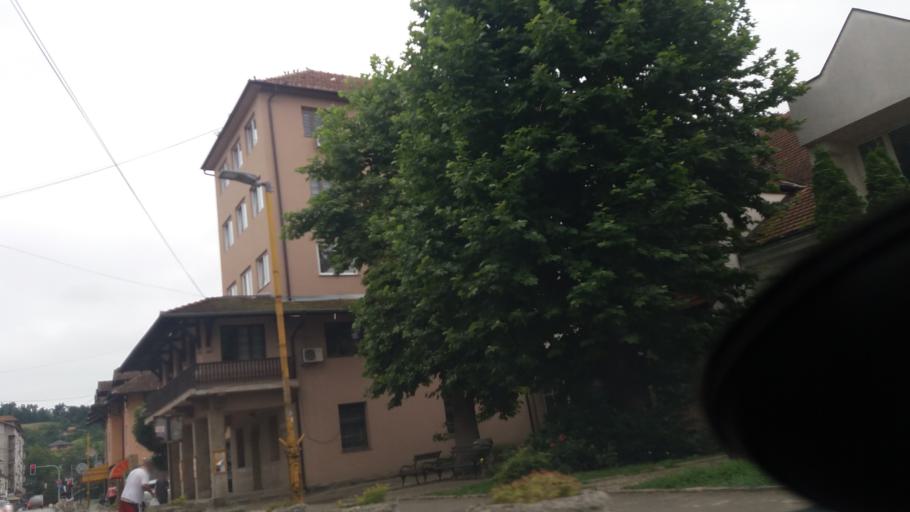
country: RS
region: Central Serbia
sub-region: Kolubarski Okrug
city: Ljig
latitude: 44.2263
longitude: 20.2393
